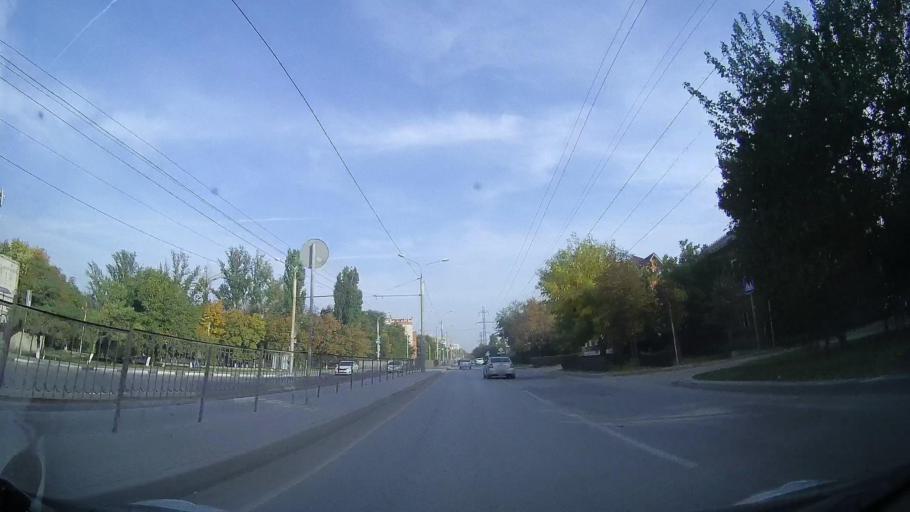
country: RU
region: Rostov
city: Imeni Chkalova
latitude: 47.2851
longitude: 39.7477
